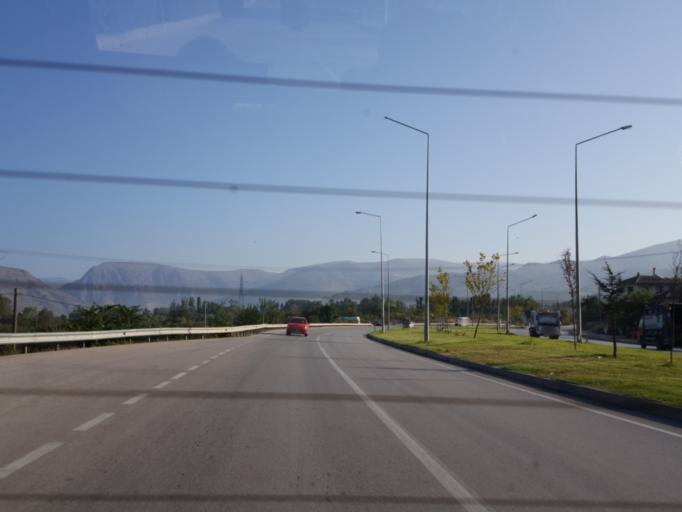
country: TR
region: Amasya
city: Amasya
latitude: 40.5857
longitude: 35.7947
